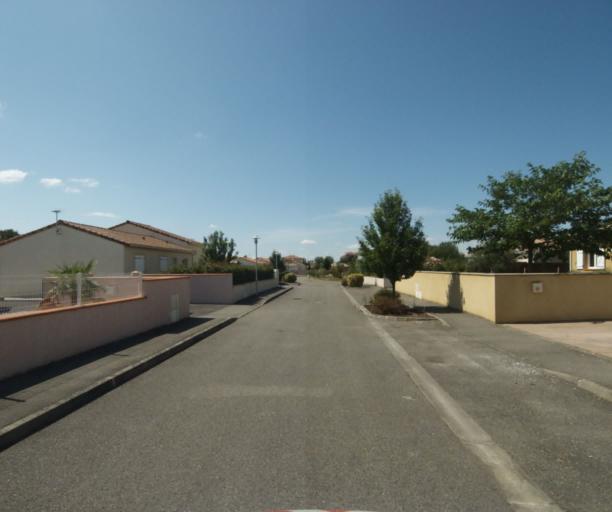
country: FR
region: Midi-Pyrenees
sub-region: Departement de la Haute-Garonne
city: Revel
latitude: 43.4635
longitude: 2.0130
